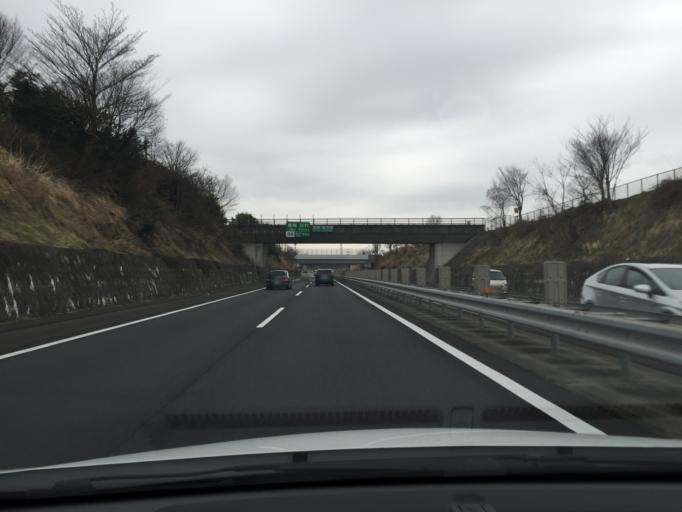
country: JP
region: Saitama
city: Hanno
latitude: 35.8037
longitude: 139.3351
